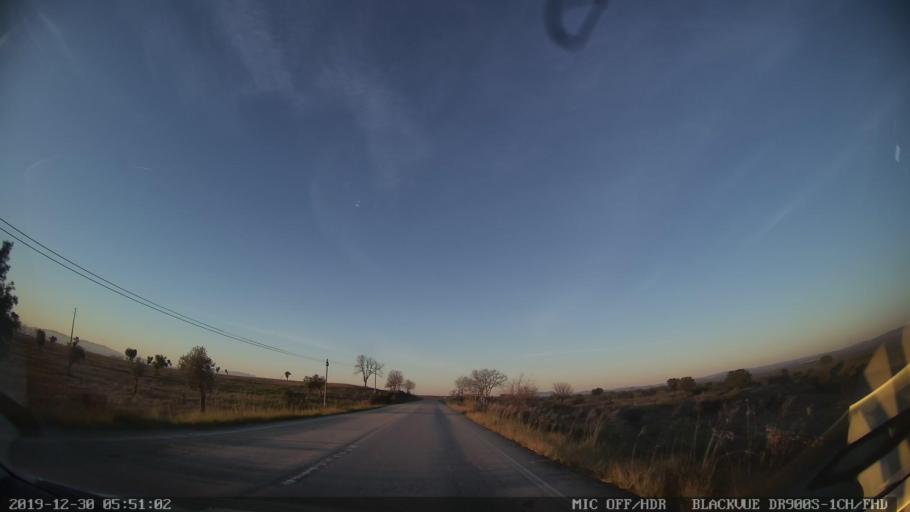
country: PT
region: Castelo Branco
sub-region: Idanha-A-Nova
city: Idanha-a-Nova
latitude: 39.9896
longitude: -7.2424
